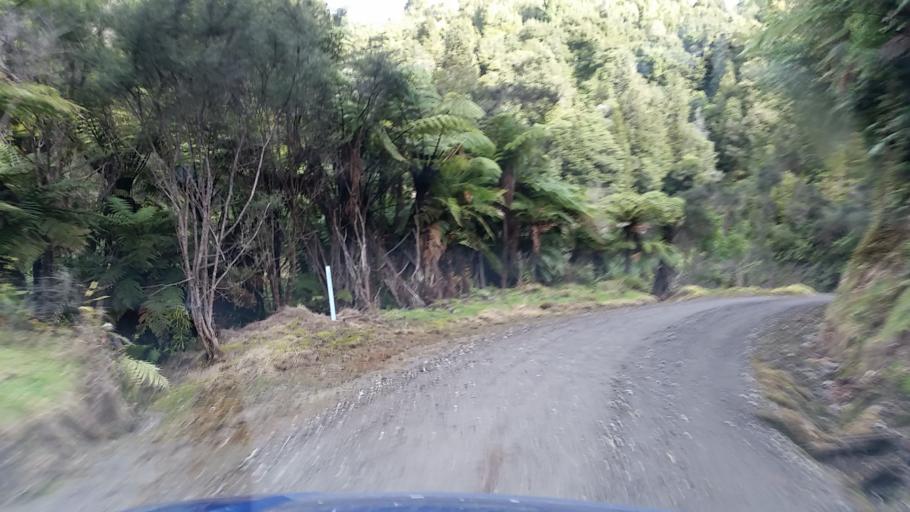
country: NZ
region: Taranaki
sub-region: South Taranaki District
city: Eltham
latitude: -39.2795
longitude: 174.7567
